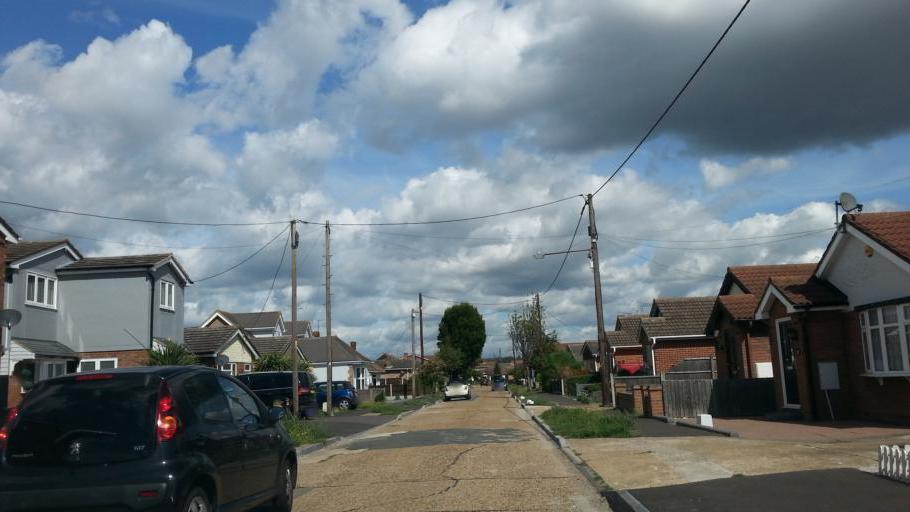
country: GB
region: England
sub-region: Essex
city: Canvey Island
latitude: 51.5212
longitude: 0.5850
